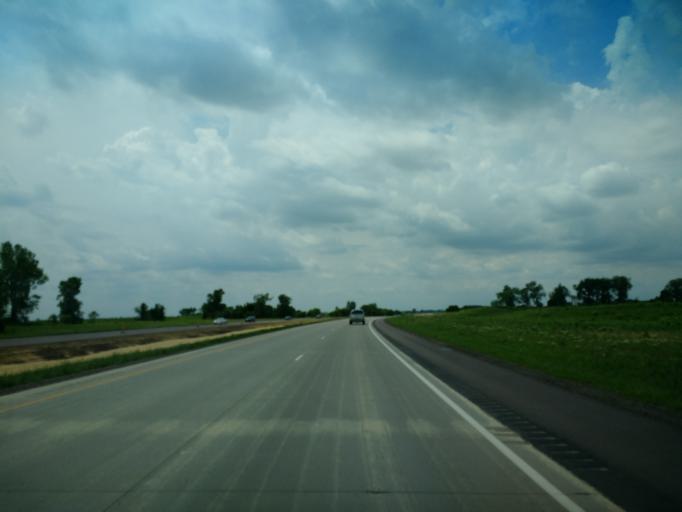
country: US
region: Minnesota
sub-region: Cottonwood County
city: Windom
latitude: 43.9017
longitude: -95.0641
